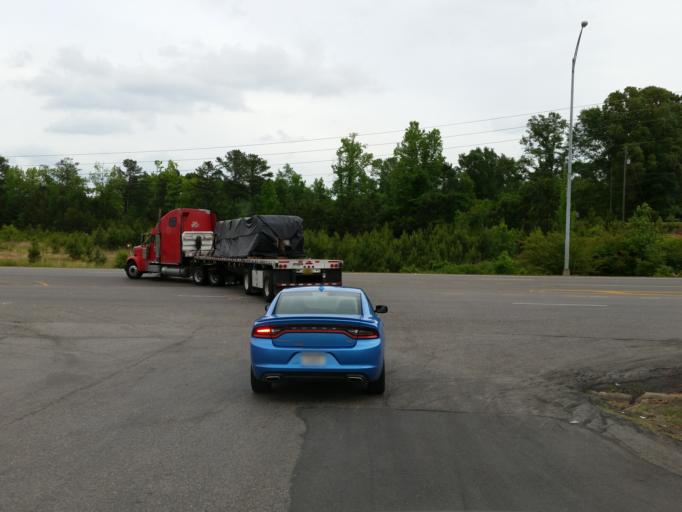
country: US
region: Alabama
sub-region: Tuscaloosa County
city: Holt
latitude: 33.1728
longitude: -87.4778
